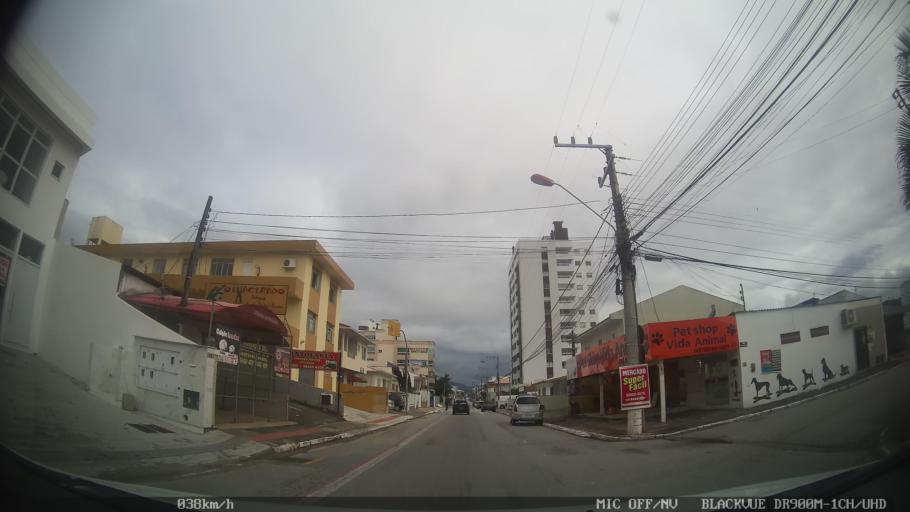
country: BR
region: Santa Catarina
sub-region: Sao Jose
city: Campinas
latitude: -27.5560
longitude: -48.6260
